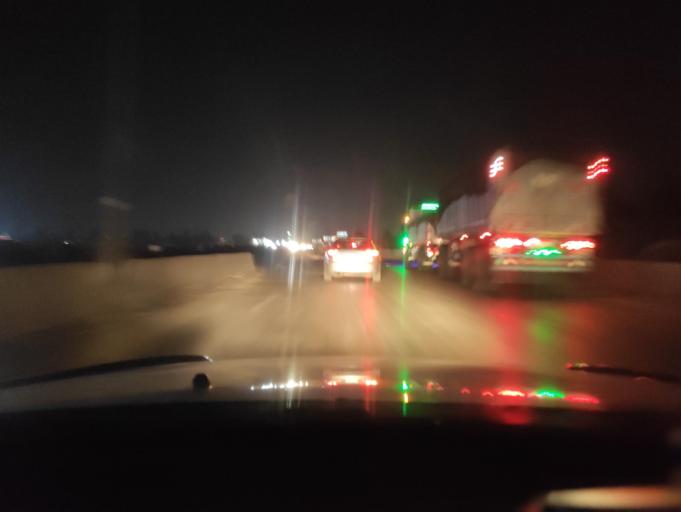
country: EG
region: Muhafazat al Qalyubiyah
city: Banha
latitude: 30.5042
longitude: 31.1626
